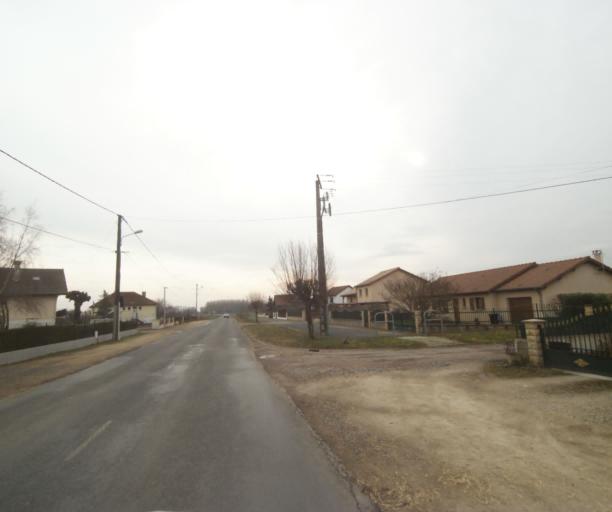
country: FR
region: Champagne-Ardenne
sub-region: Departement de la Haute-Marne
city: Villiers-en-Lieu
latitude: 48.6801
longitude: 4.8851
